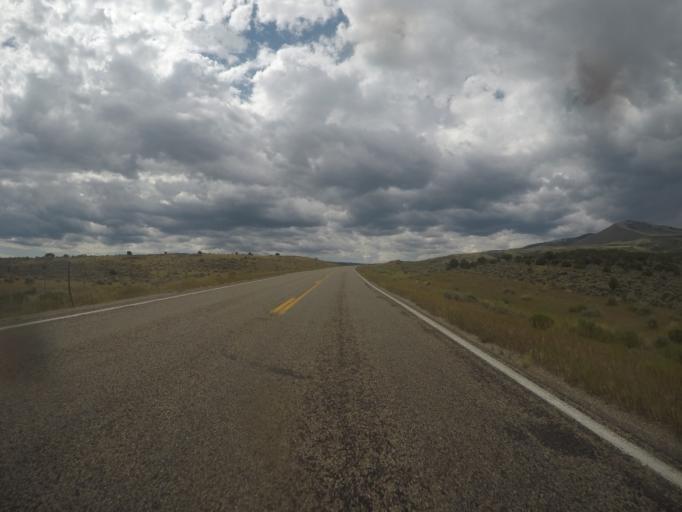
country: US
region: Utah
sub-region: Daggett County
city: Manila
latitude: 41.0025
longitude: -109.8400
